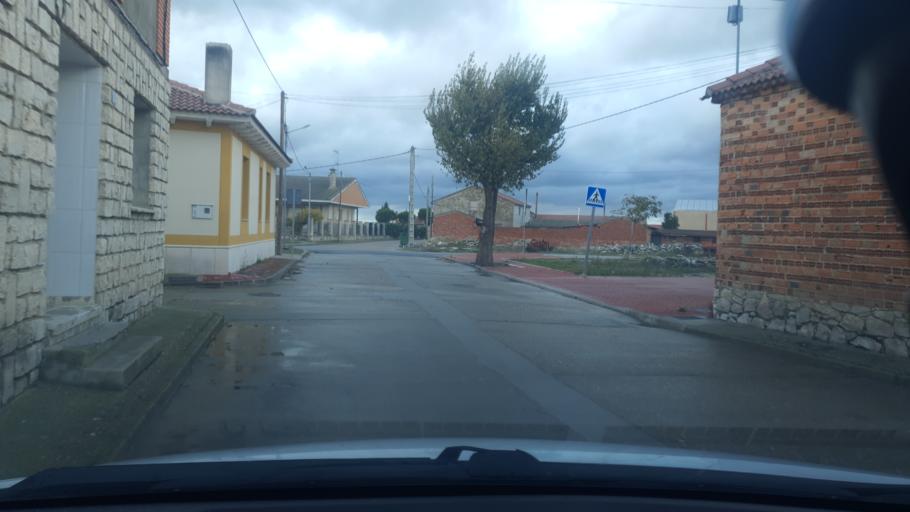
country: ES
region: Castille and Leon
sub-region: Provincia de Segovia
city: Sanchonuno
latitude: 41.2902
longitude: -4.3280
